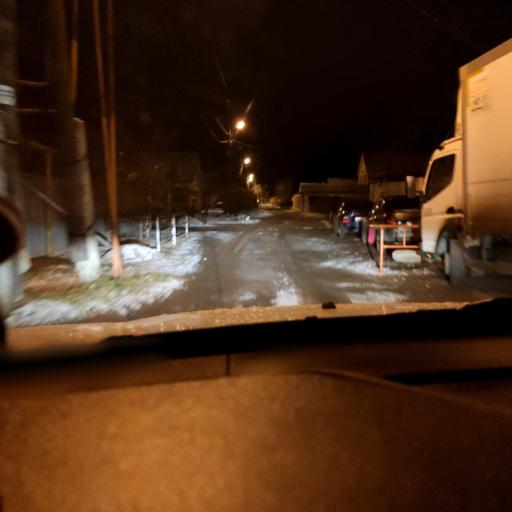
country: RU
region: Samara
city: Samara
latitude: 53.1825
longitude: 50.2327
